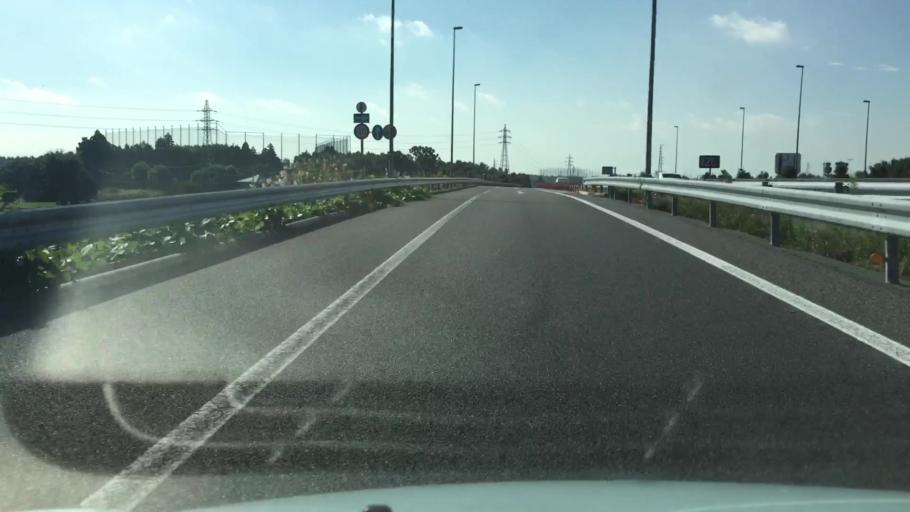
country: JP
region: Tochigi
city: Mooka
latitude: 36.4455
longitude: 139.9689
